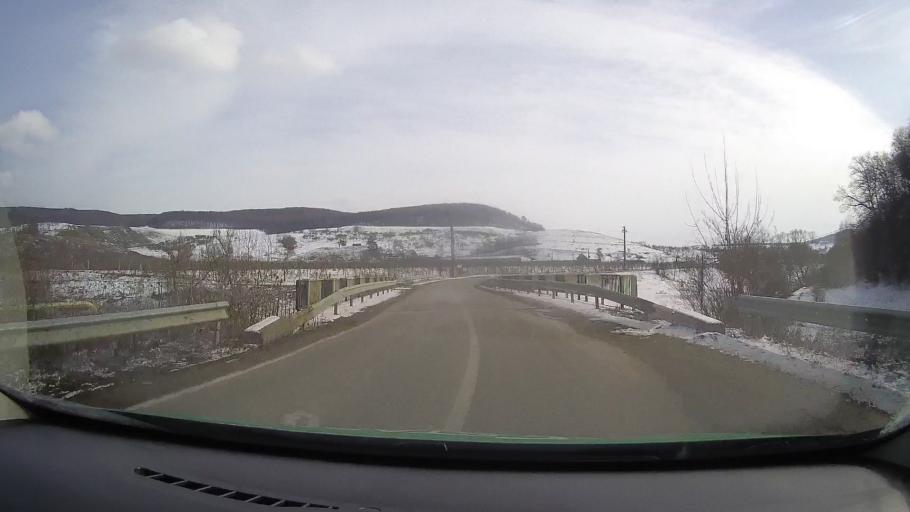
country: RO
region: Mures
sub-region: Comuna Apold
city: Apold
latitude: 46.1394
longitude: 24.8195
